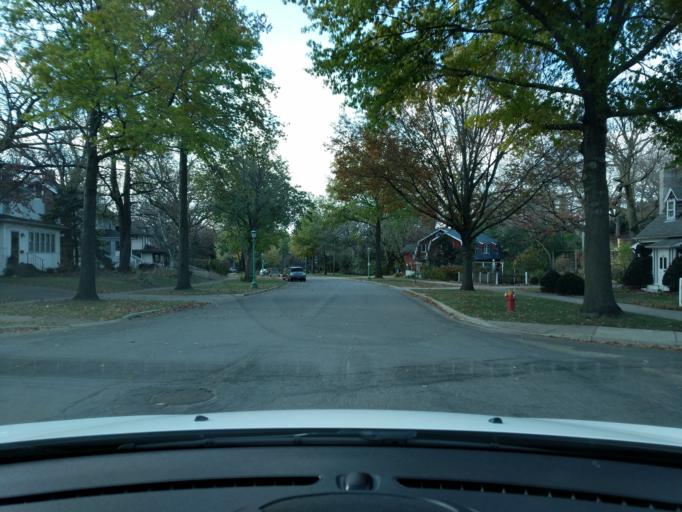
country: US
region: Minnesota
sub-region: Ramsey County
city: Lauderdale
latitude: 44.9802
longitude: -93.1980
